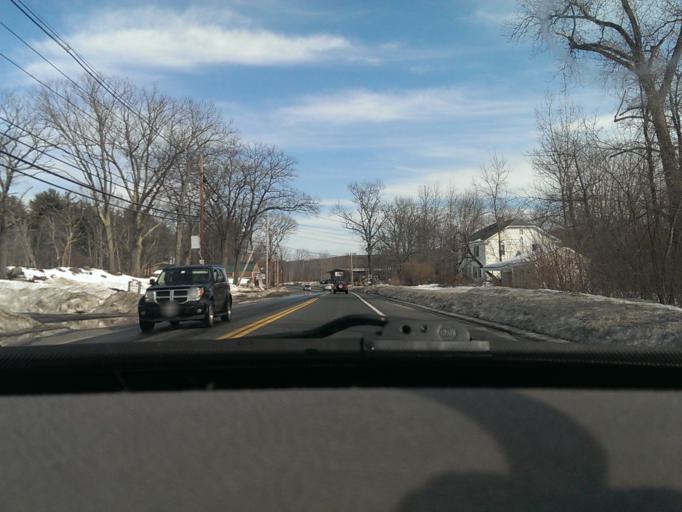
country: US
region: Massachusetts
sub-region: Hampden County
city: Three Rivers
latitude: 42.1537
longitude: -72.3712
